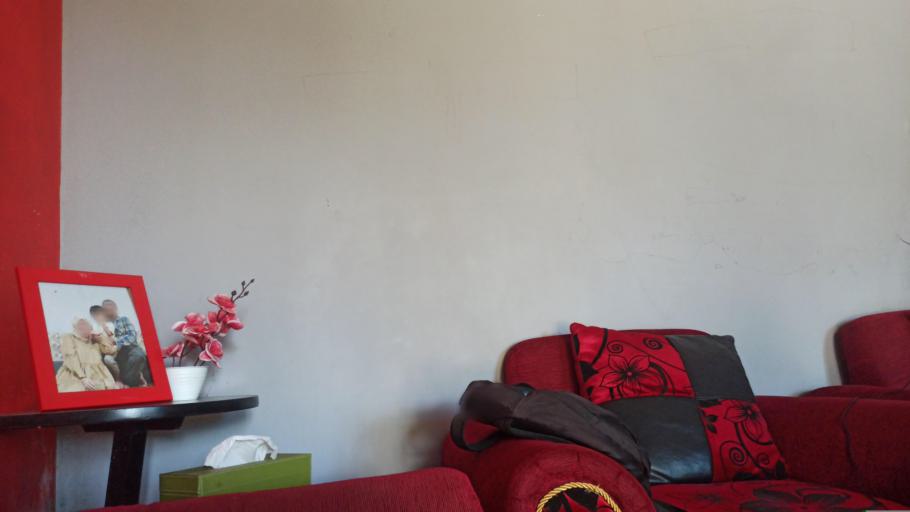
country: ID
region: West Kalimantan
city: Mempawah
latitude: 0.3665
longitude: 108.9548
